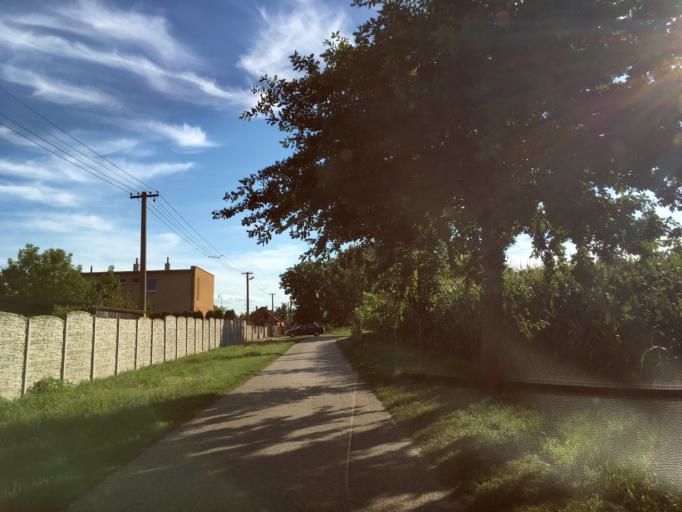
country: SK
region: Nitriansky
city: Svodin
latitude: 47.8989
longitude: 18.4070
